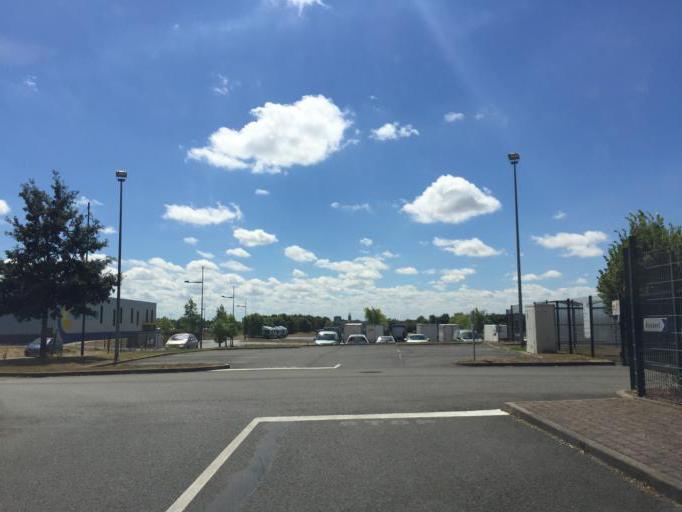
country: FR
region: Auvergne
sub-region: Departement de l'Allier
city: Avermes
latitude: 46.5949
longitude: 3.3284
